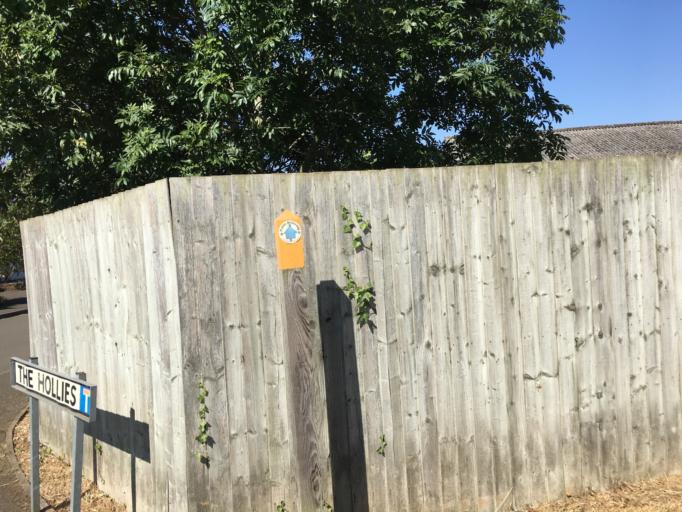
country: GB
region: England
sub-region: Warwickshire
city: Rugby
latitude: 52.3996
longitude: -1.2225
